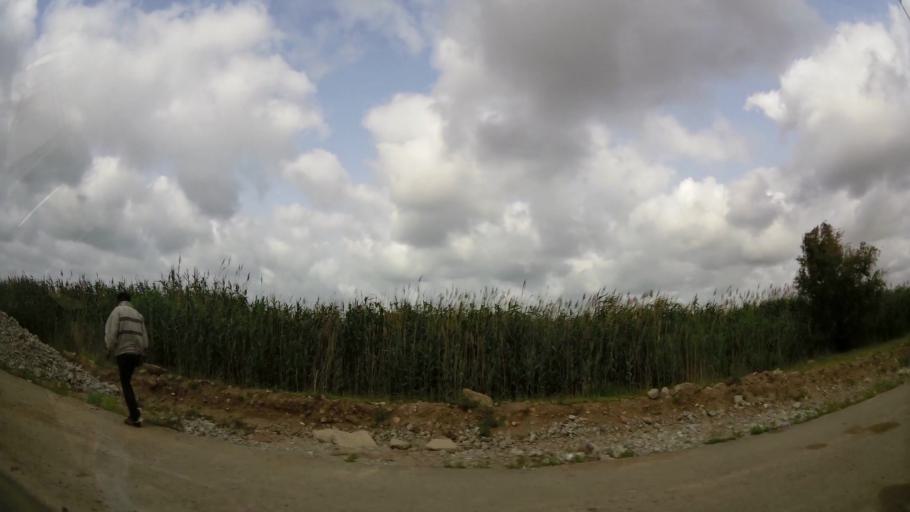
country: MA
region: Oriental
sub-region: Nador
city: Nador
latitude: 35.1550
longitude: -2.9069
